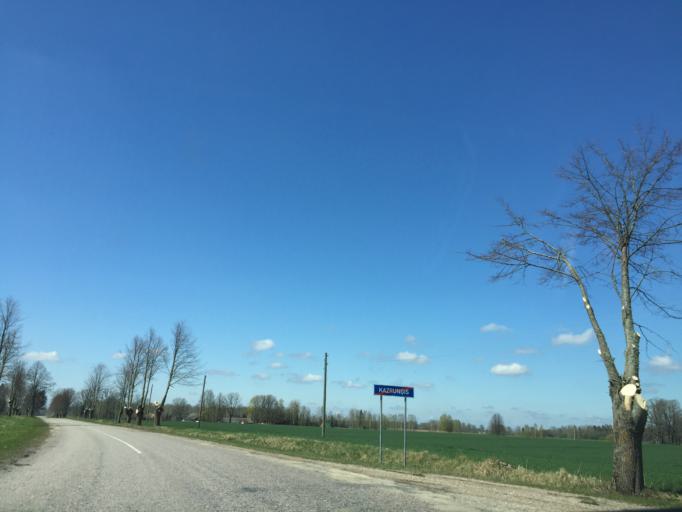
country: LV
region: Strenci
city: Seda
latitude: 57.5616
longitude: 25.8250
